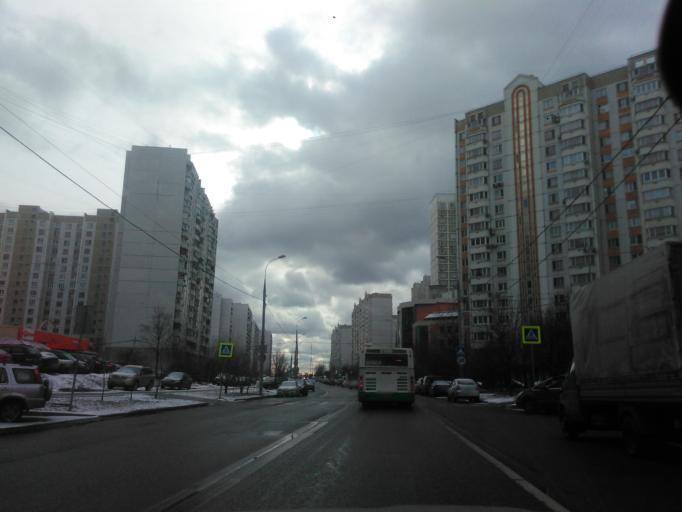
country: RU
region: Moskovskaya
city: Krasnogorsk
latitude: 55.8470
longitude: 37.3452
